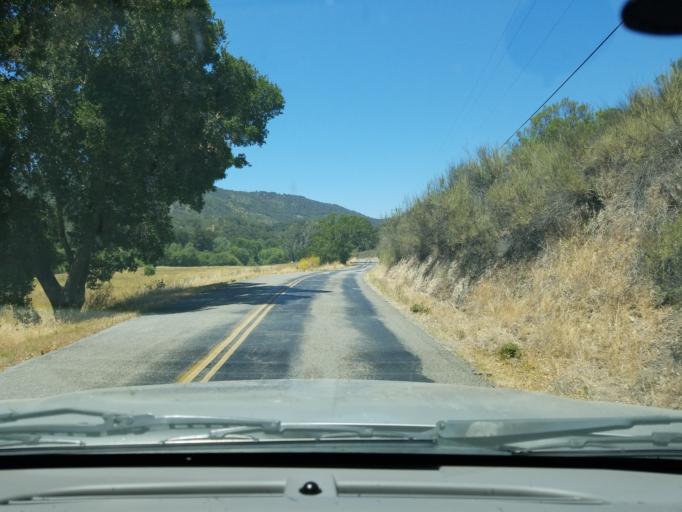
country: US
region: California
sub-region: Monterey County
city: Carmel Valley Village
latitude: 36.4436
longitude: -121.6616
